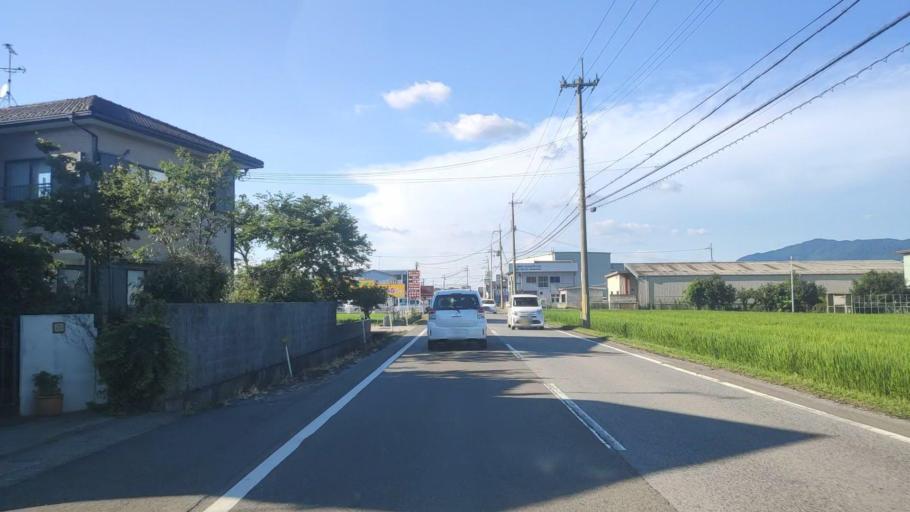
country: JP
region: Shiga Prefecture
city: Youkaichi
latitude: 35.0819
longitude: 136.2499
